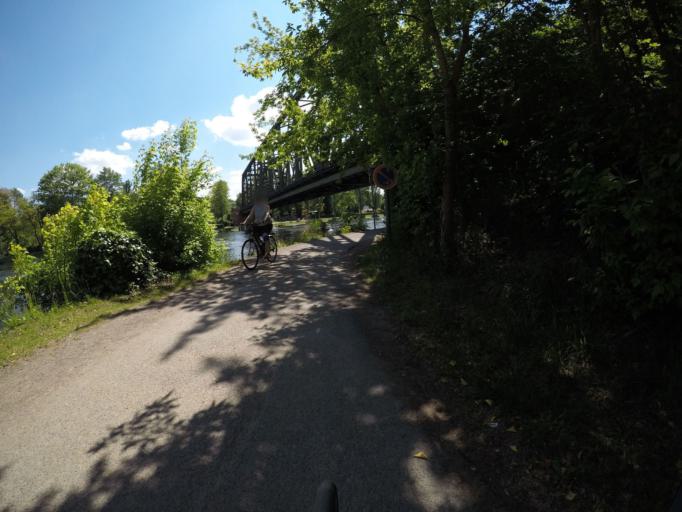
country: DE
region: Brandenburg
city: Michendorf
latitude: 52.3440
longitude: 12.9809
